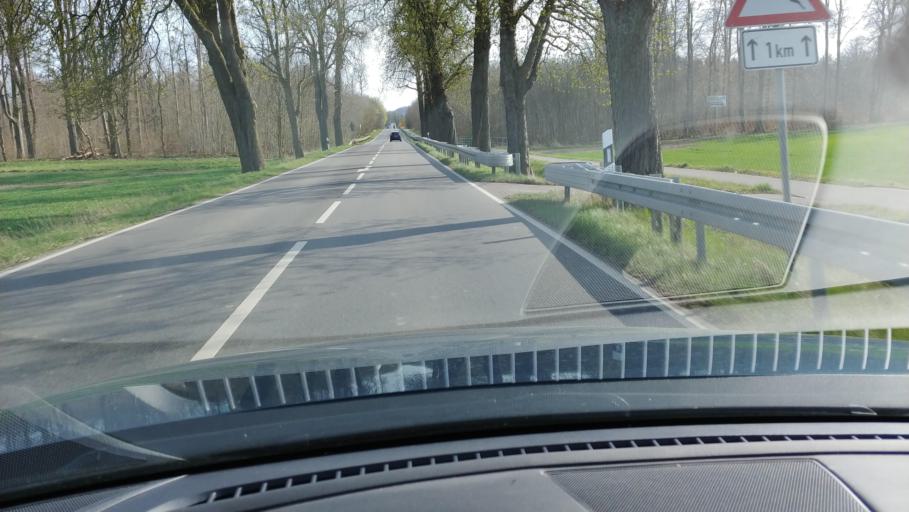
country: DE
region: Mecklenburg-Vorpommern
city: Lubstorf
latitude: 53.7362
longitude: 11.4063
